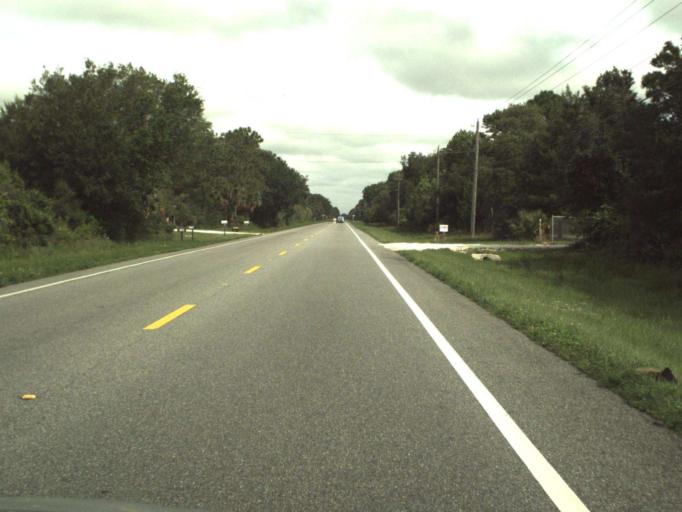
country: US
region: Florida
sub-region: Seminole County
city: Geneva
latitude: 28.7624
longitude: -81.1474
